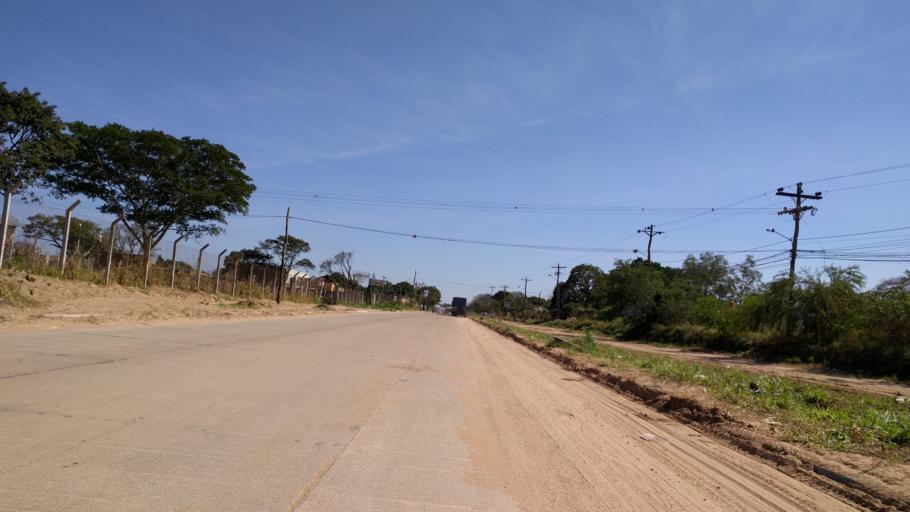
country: BO
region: Santa Cruz
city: Santa Cruz de la Sierra
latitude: -17.8410
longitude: -63.2339
